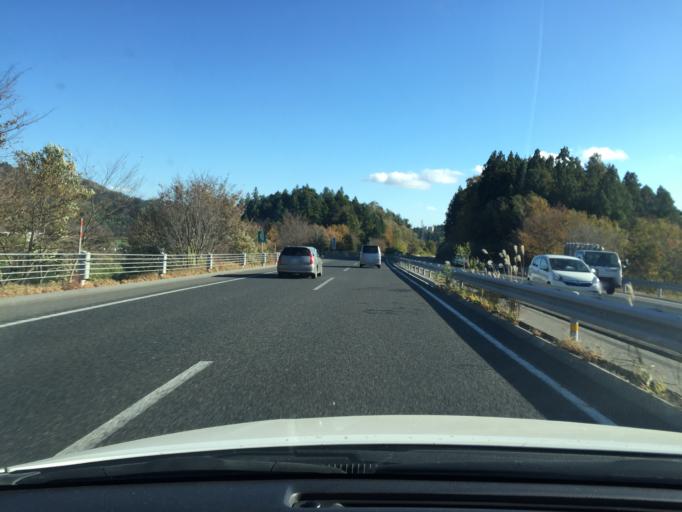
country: JP
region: Fukushima
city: Funehikimachi-funehiki
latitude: 37.3044
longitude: 140.6131
